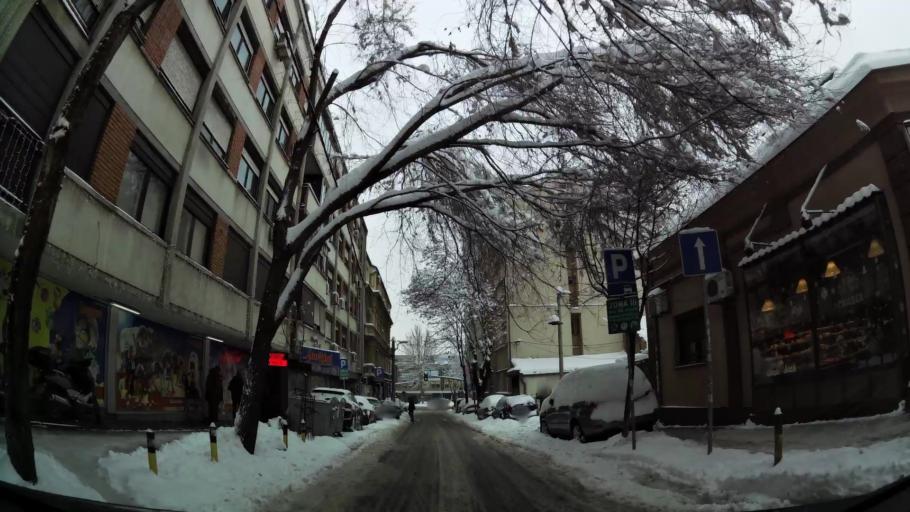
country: RS
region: Central Serbia
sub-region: Belgrade
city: Vracar
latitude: 44.8029
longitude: 20.4794
